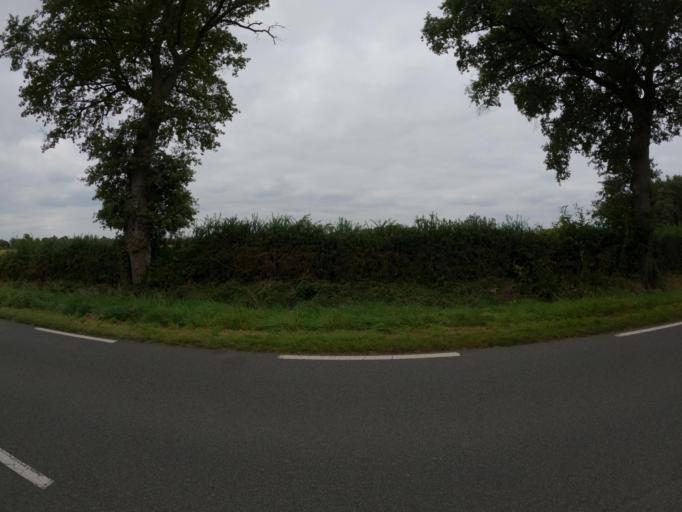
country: FR
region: Poitou-Charentes
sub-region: Departement de la Vienne
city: Availles-Limouzine
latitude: 46.0800
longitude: 0.5897
